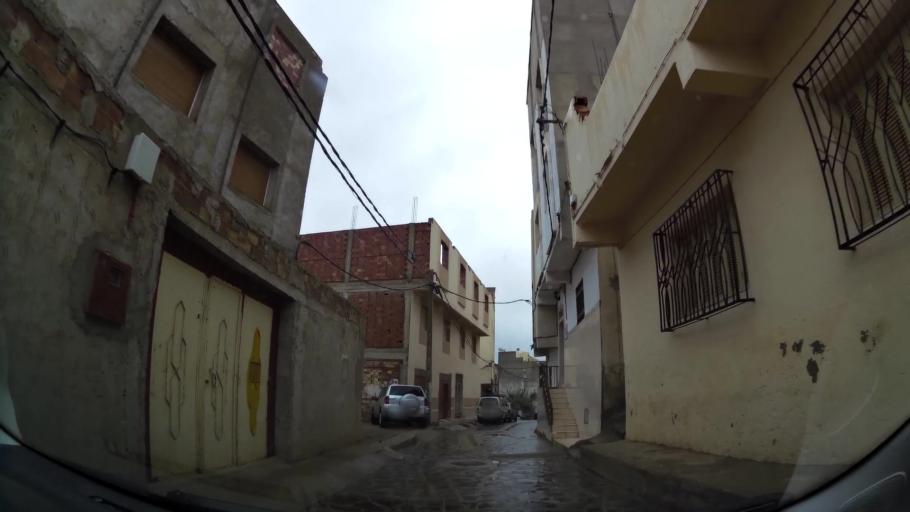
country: MA
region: Oriental
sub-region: Nador
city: Nador
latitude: 35.1763
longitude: -2.9373
